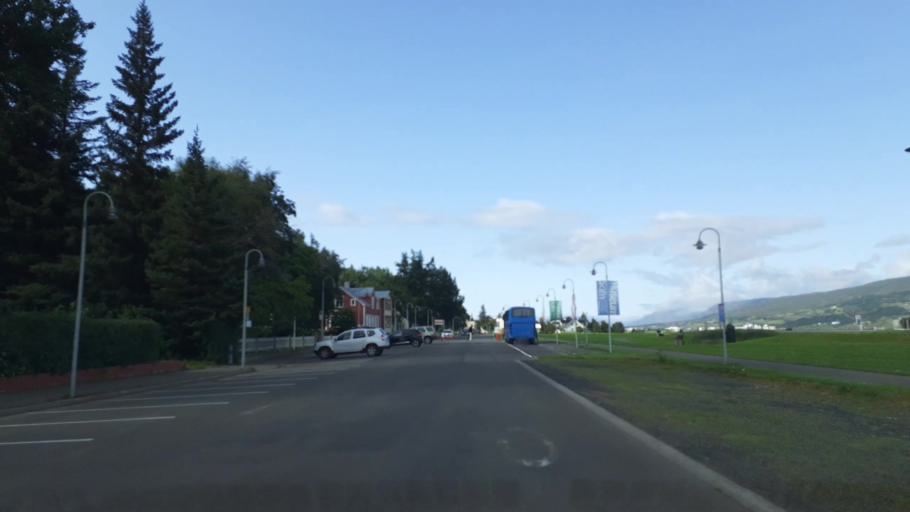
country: IS
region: Northeast
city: Akureyri
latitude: 65.6661
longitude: -18.0847
